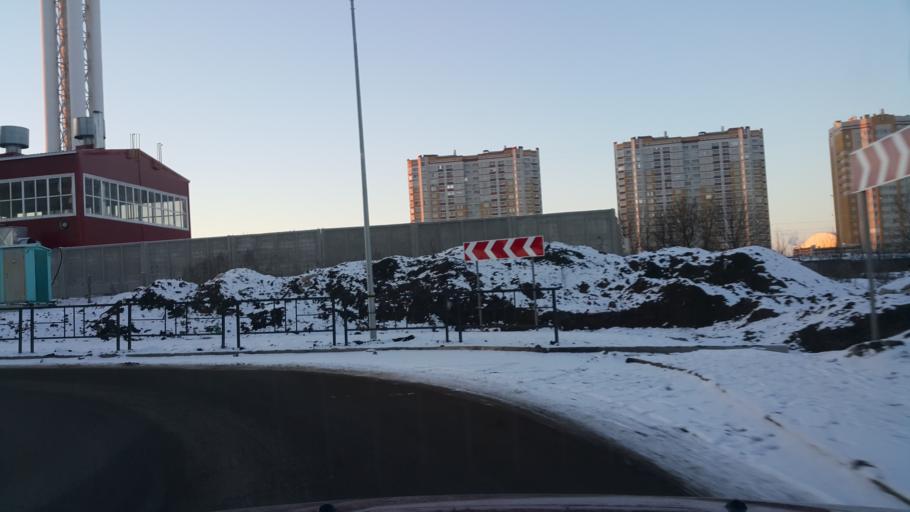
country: RU
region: Tambov
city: Tambov
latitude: 52.7601
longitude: 41.3943
